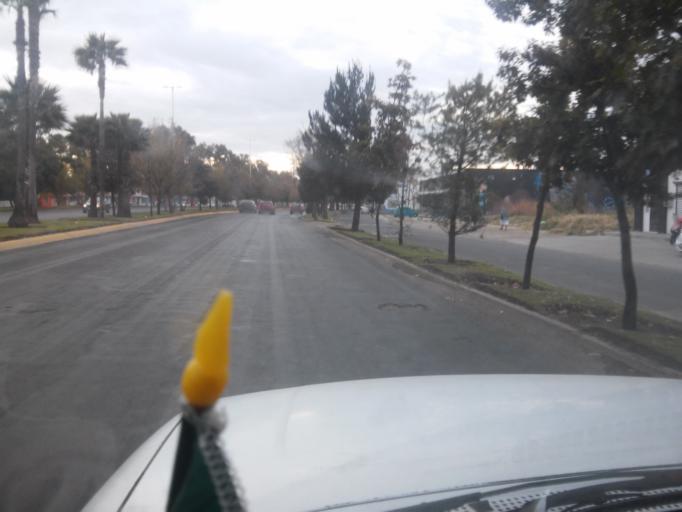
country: MX
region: Durango
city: Victoria de Durango
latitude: 24.0065
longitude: -104.6576
